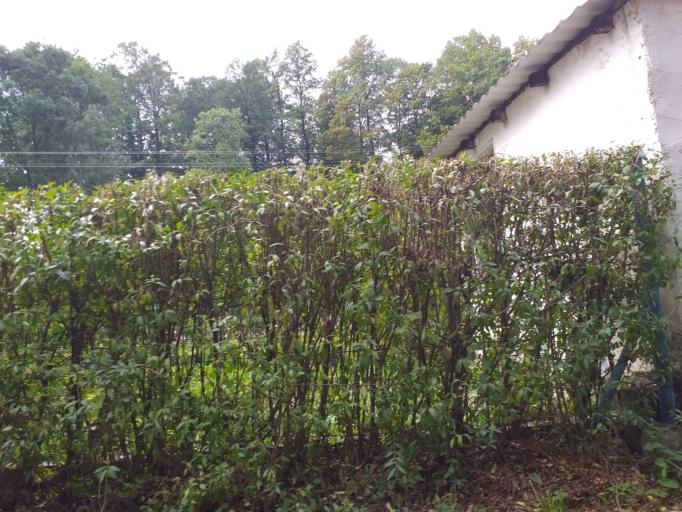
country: PL
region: Lower Silesian Voivodeship
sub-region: Powiat lubanski
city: Lesna
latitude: 51.0121
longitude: 15.3098
